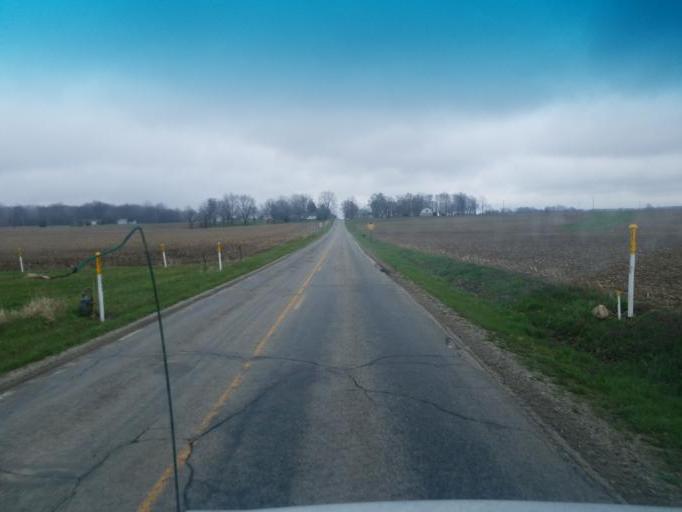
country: US
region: Ohio
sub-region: Richland County
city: Shelby
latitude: 40.9139
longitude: -82.6311
